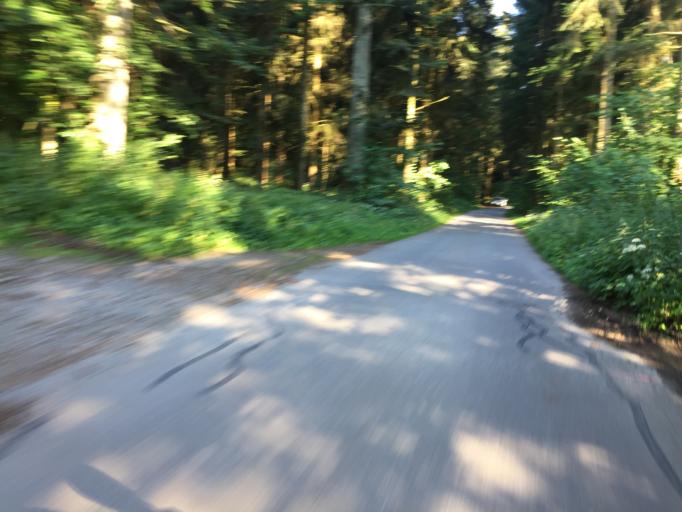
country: CH
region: Bern
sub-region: Bern-Mittelland District
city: Niederwichtrach
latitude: 46.8314
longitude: 7.5863
